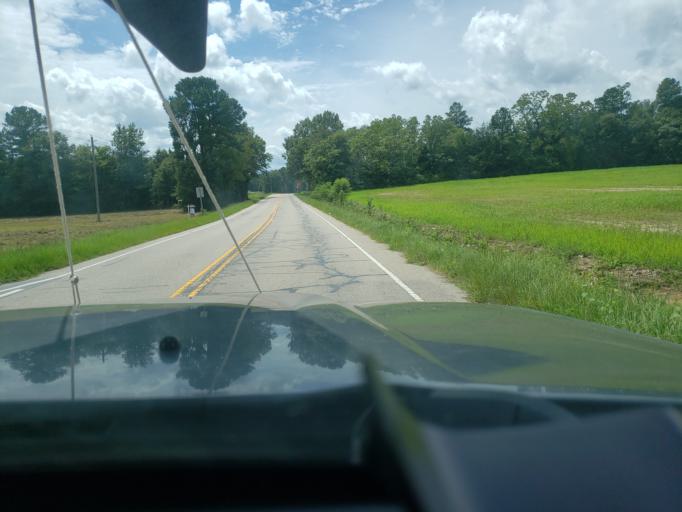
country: US
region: North Carolina
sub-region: Wake County
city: Rolesville
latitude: 35.8908
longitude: -78.4318
